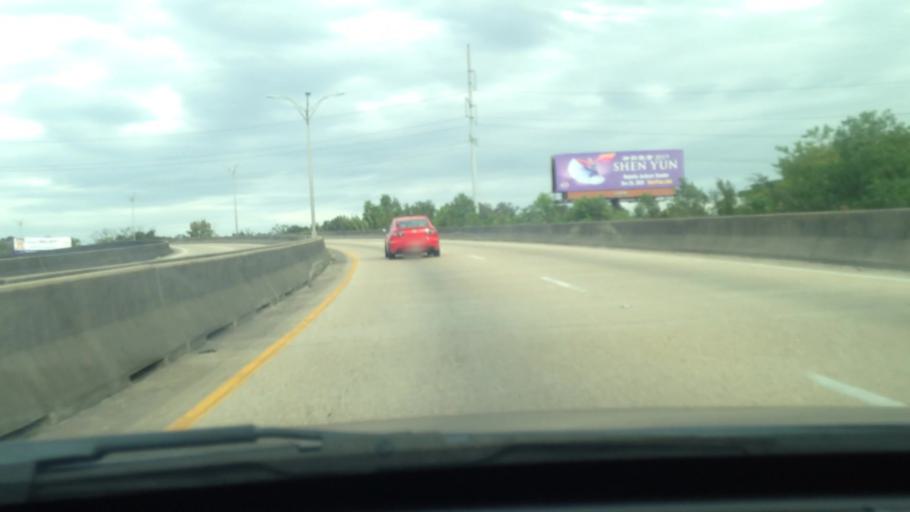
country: US
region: Louisiana
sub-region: Jefferson Parish
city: River Ridge
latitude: 29.9718
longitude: -90.2047
